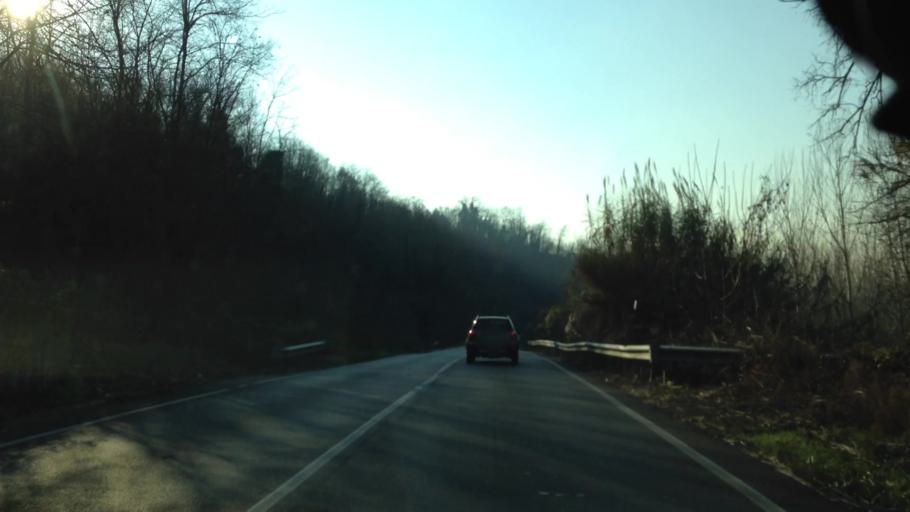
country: IT
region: Piedmont
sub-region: Provincia di Alessandria
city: Masio
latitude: 44.8702
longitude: 8.4352
